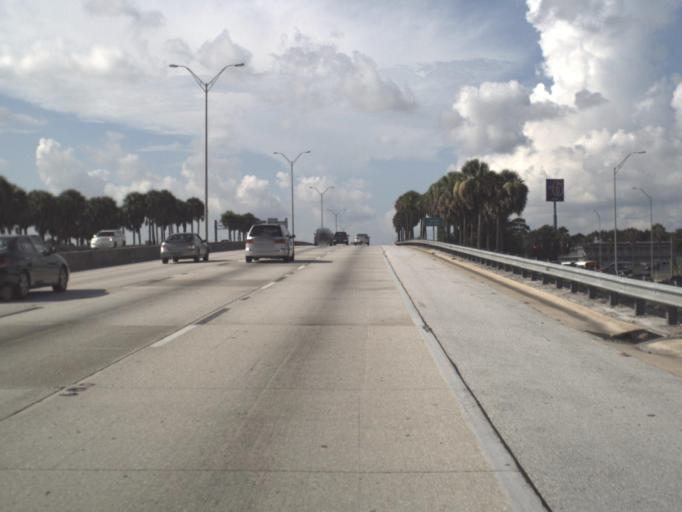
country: US
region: Florida
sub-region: Hillsborough County
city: University
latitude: 28.0565
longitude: -82.4549
